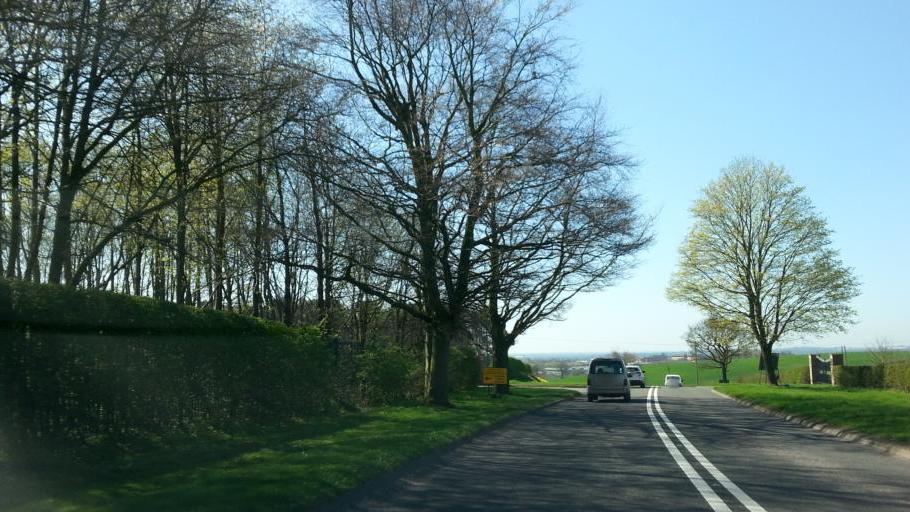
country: GB
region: England
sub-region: Staffordshire
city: Stafford
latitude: 52.8250
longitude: -2.0691
